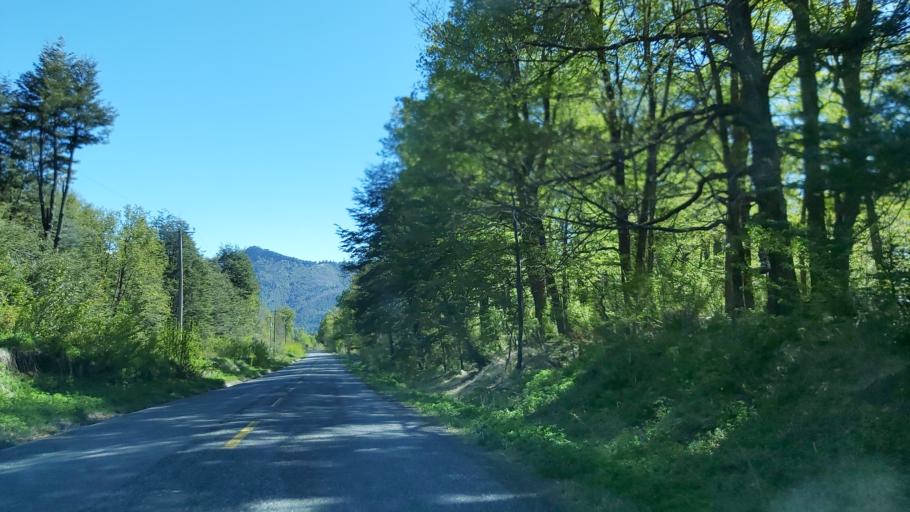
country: CL
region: Araucania
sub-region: Provincia de Cautin
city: Vilcun
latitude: -38.4707
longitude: -71.5248
